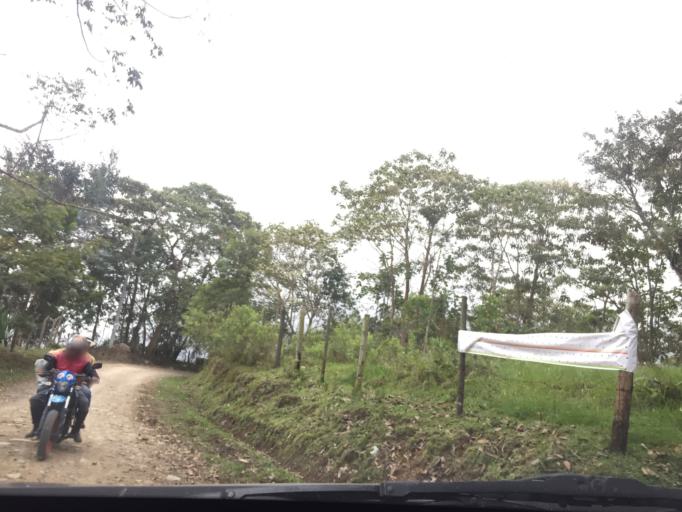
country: CO
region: Cundinamarca
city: Bojaca
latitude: 4.6862
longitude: -74.3765
